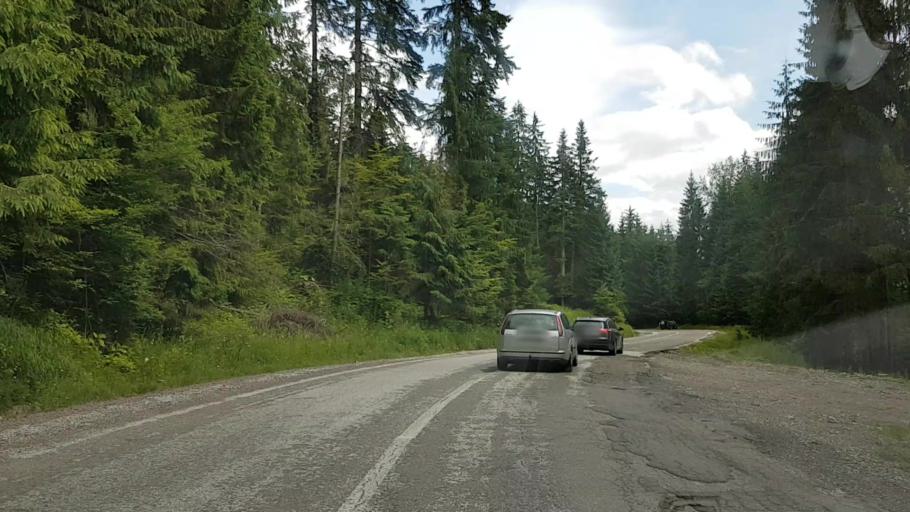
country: RO
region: Neamt
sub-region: Comuna Pangarati
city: Pangarati
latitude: 46.9724
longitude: 26.1171
